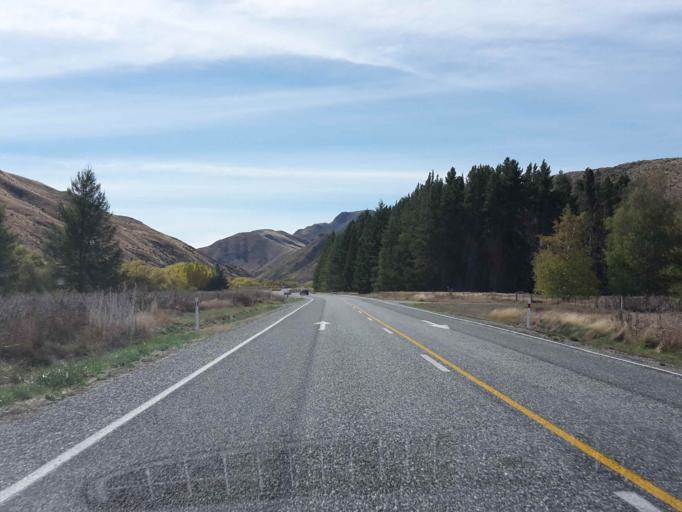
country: NZ
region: Otago
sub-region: Queenstown-Lakes District
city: Wanaka
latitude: -44.6380
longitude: 169.5094
